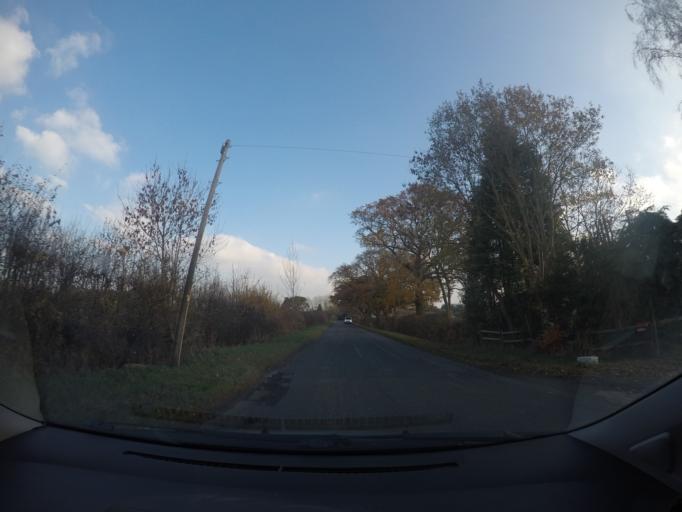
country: GB
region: England
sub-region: City of York
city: Huntington
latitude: 53.9994
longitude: -1.0238
